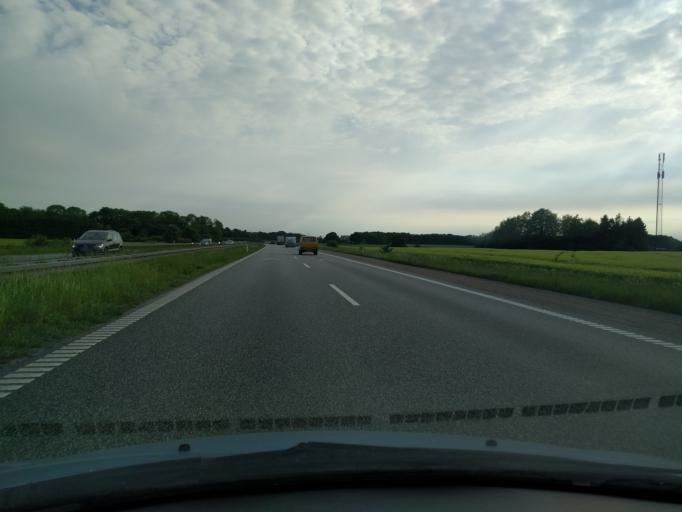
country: DK
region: Zealand
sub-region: Koge Kommune
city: Ejby
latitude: 55.4247
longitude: 12.1101
